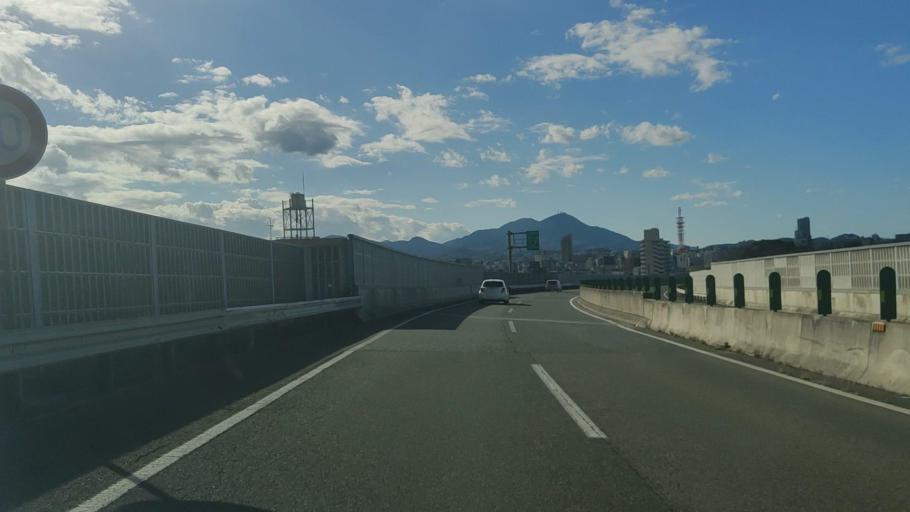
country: JP
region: Fukuoka
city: Kitakyushu
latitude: 33.8796
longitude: 130.9017
